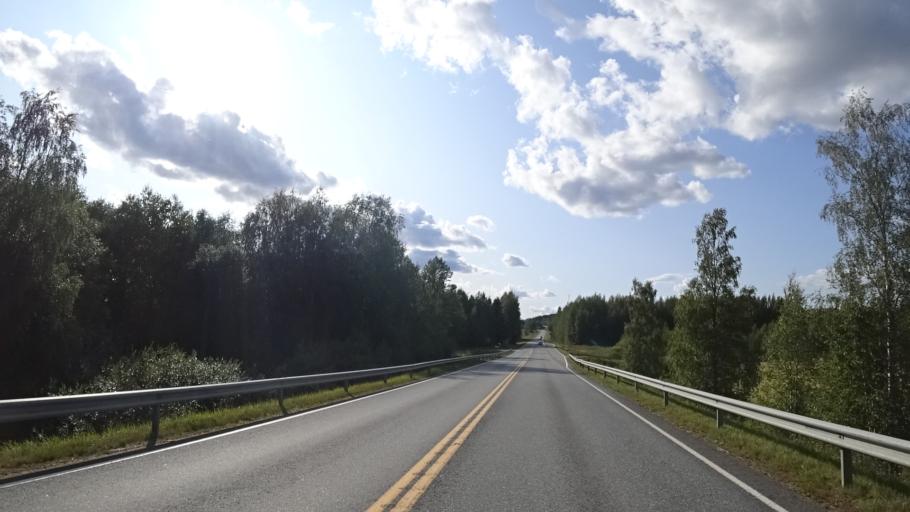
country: FI
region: North Karelia
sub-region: Keski-Karjala
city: Kitee
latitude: 62.0898
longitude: 29.9754
